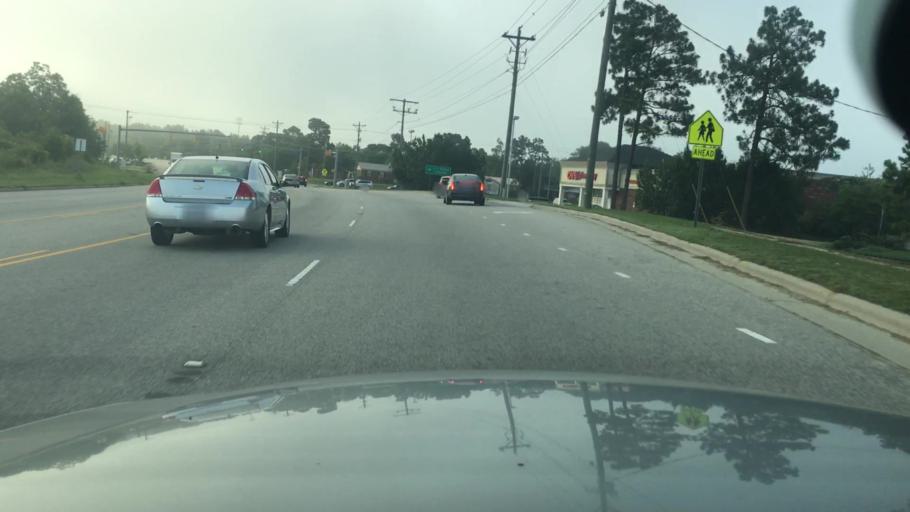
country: US
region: North Carolina
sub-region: Cumberland County
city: Hope Mills
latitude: 35.0047
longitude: -78.9177
